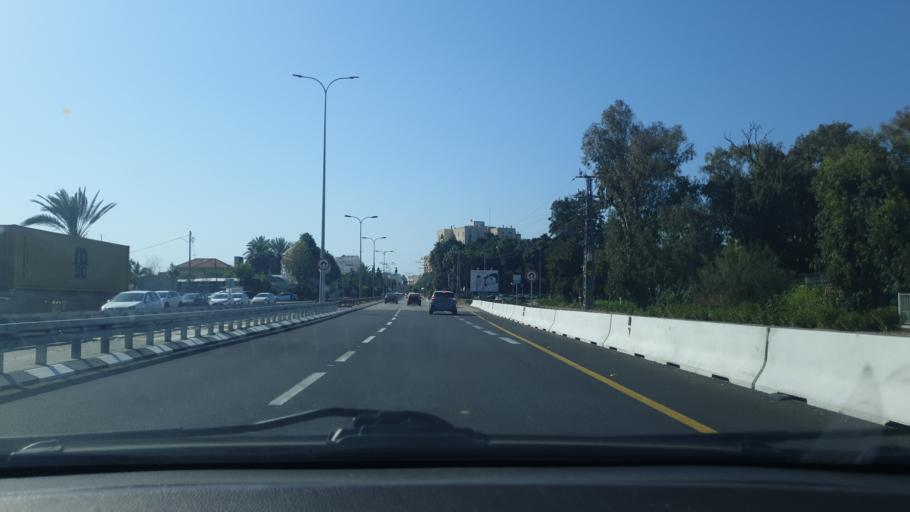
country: IL
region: Tel Aviv
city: Azor
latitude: 32.0443
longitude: 34.8150
